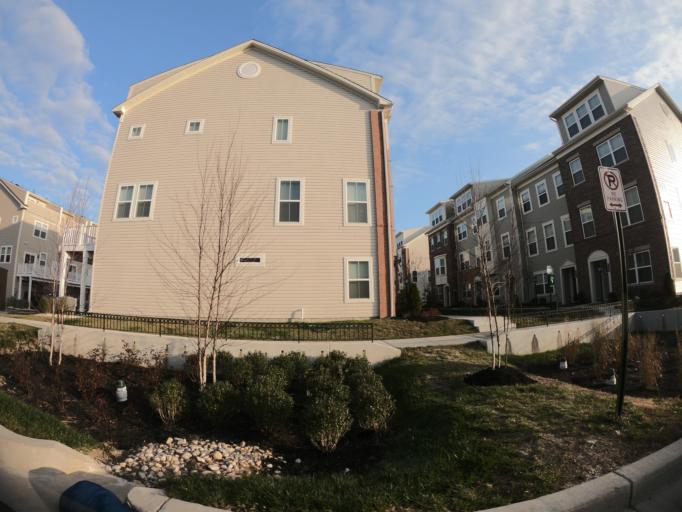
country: US
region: Maryland
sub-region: Howard County
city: Hanover
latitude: 39.1870
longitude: -76.7403
